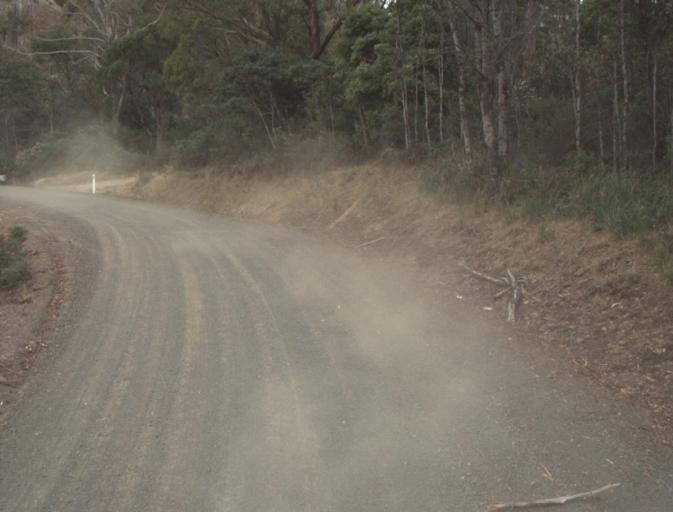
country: AU
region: Tasmania
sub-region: Northern Midlands
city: Evandale
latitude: -41.4924
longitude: 147.4326
